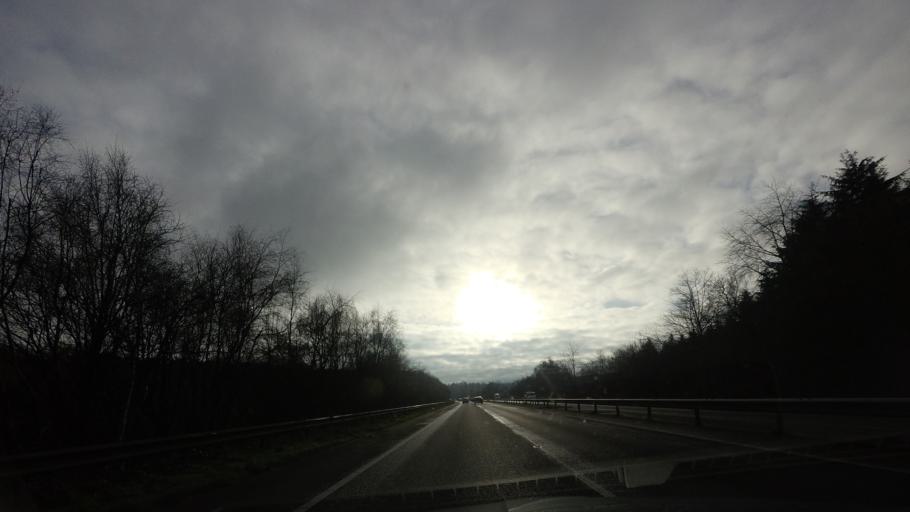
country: GB
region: England
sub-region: Kent
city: Sevenoaks
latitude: 51.2605
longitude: 0.1716
